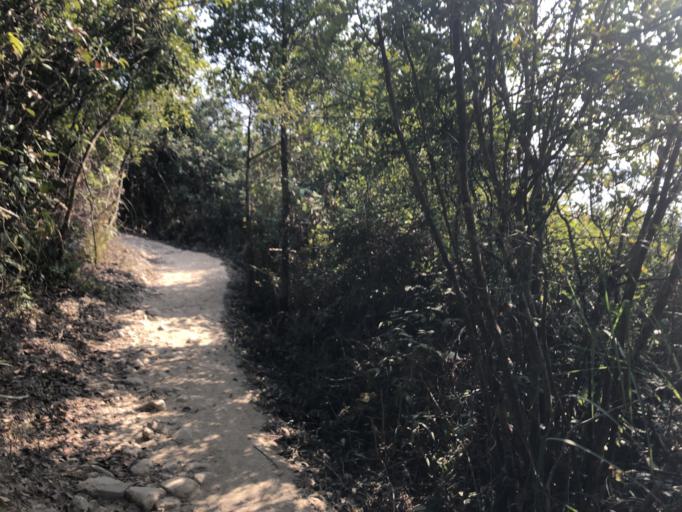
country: HK
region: Sai Kung
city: Sai Kung
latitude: 22.3645
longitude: 114.2920
